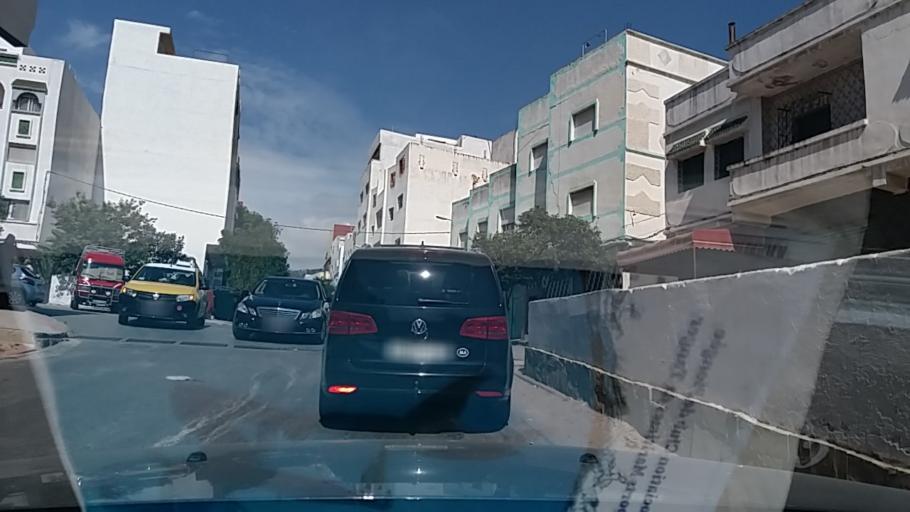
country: MA
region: Tanger-Tetouan
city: Tetouan
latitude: 35.5659
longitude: -5.4007
